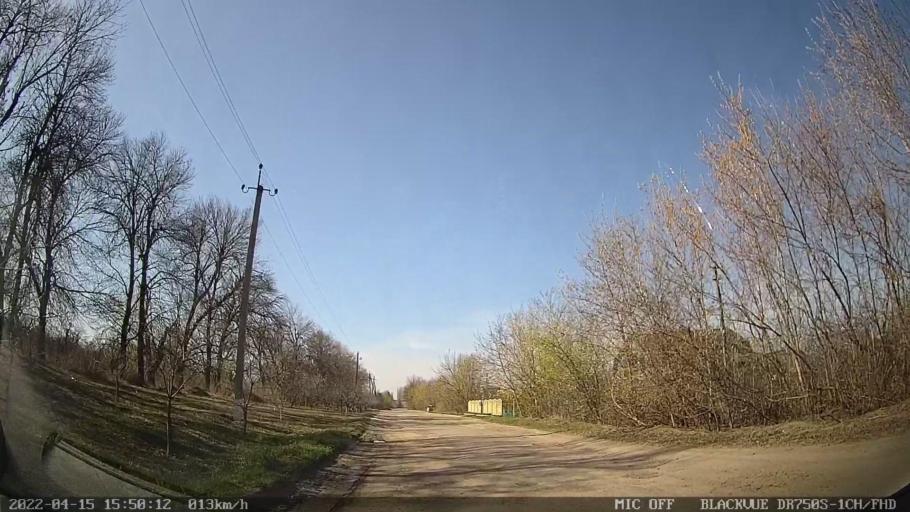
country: MD
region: Raionul Ocnita
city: Otaci
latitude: 48.3912
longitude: 27.9017
